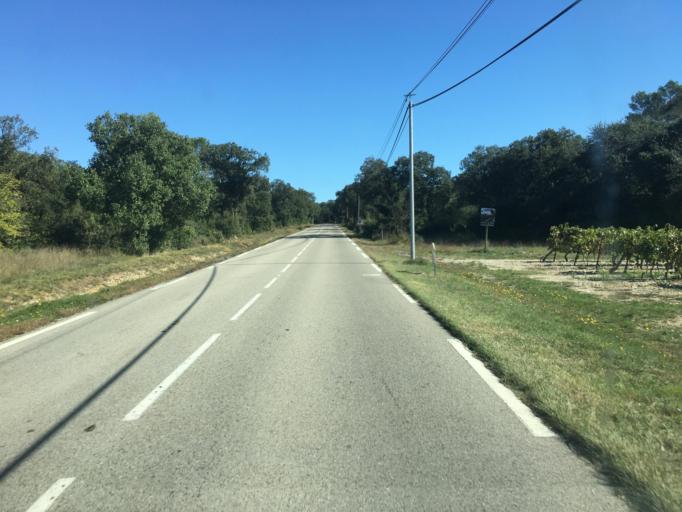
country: FR
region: Languedoc-Roussillon
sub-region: Departement du Gard
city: Quissac
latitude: 43.9206
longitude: 4.0339
